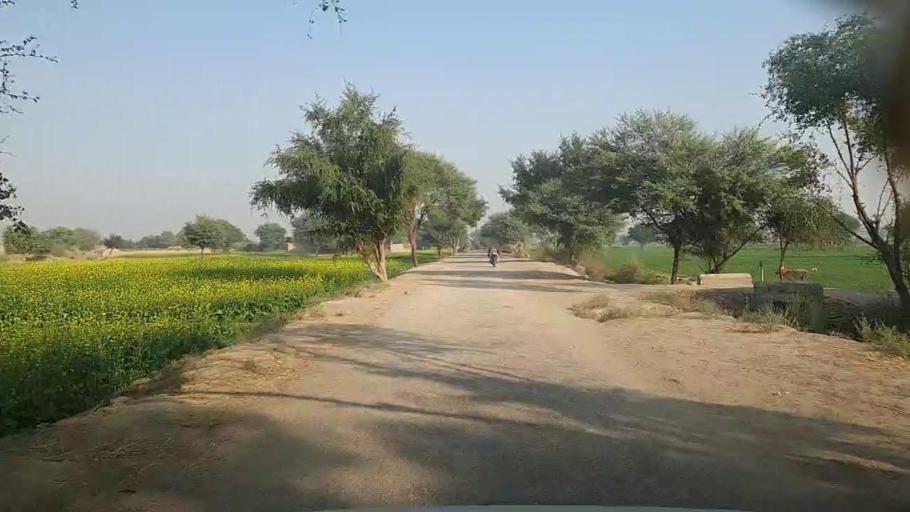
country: PK
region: Sindh
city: Kandiari
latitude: 26.7658
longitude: 68.4972
